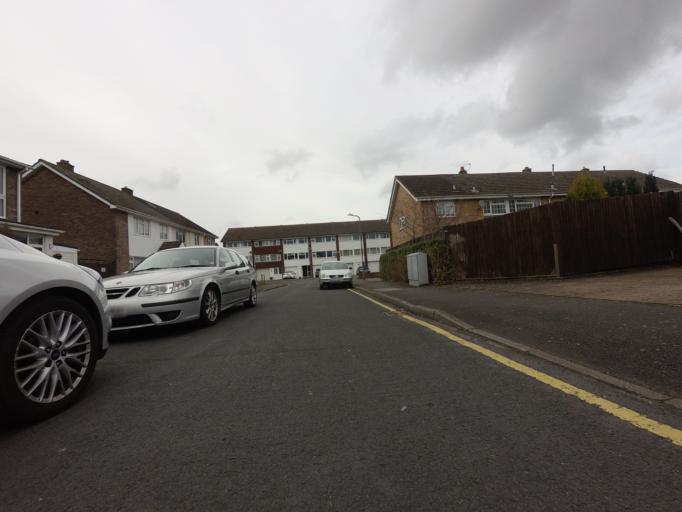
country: GB
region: England
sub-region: Kent
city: Swanley
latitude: 51.3920
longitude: 0.1669
